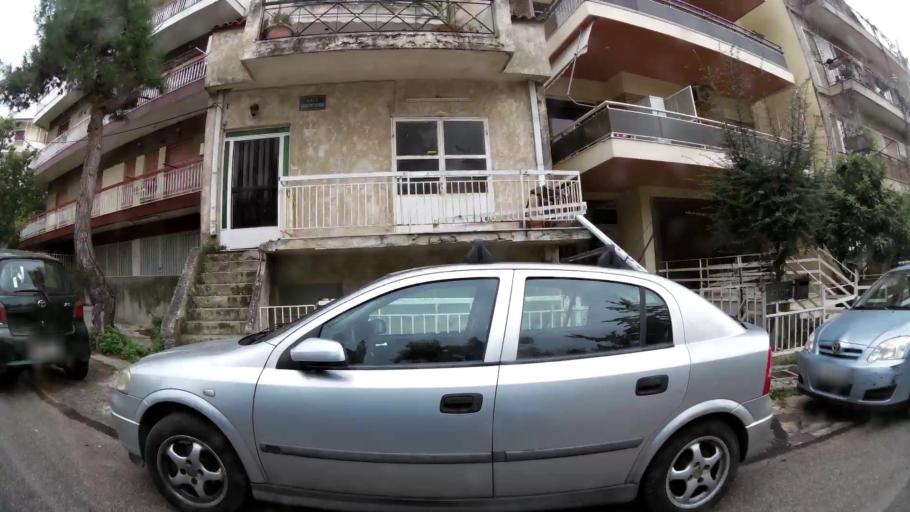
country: GR
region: Attica
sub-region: Nomarchia Athinas
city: Kaisariani
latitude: 37.9623
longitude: 23.7633
